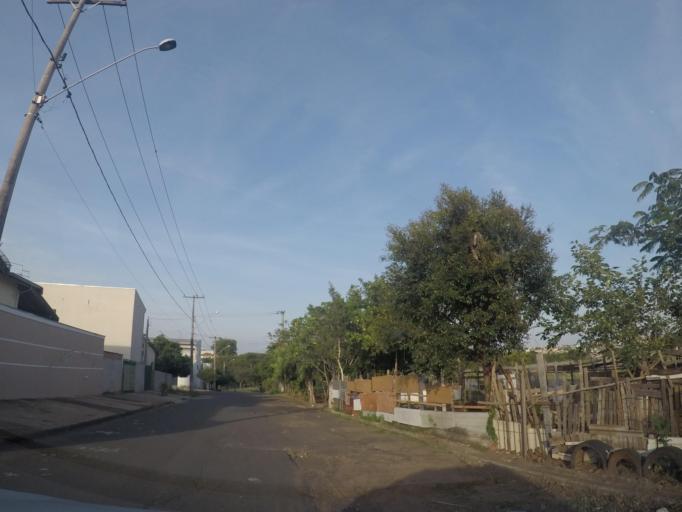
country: BR
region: Sao Paulo
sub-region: Hortolandia
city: Hortolandia
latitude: -22.8447
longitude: -47.1839
